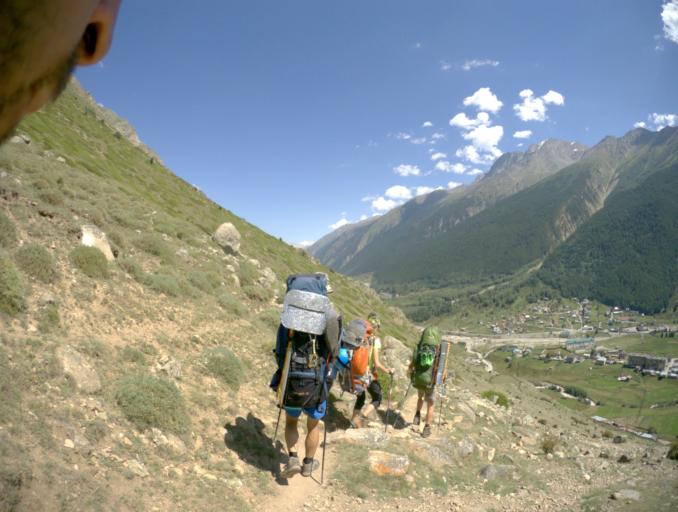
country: RU
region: Kabardino-Balkariya
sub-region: El'brusskiy Rayon
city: El'brus
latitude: 43.2629
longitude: 42.6409
